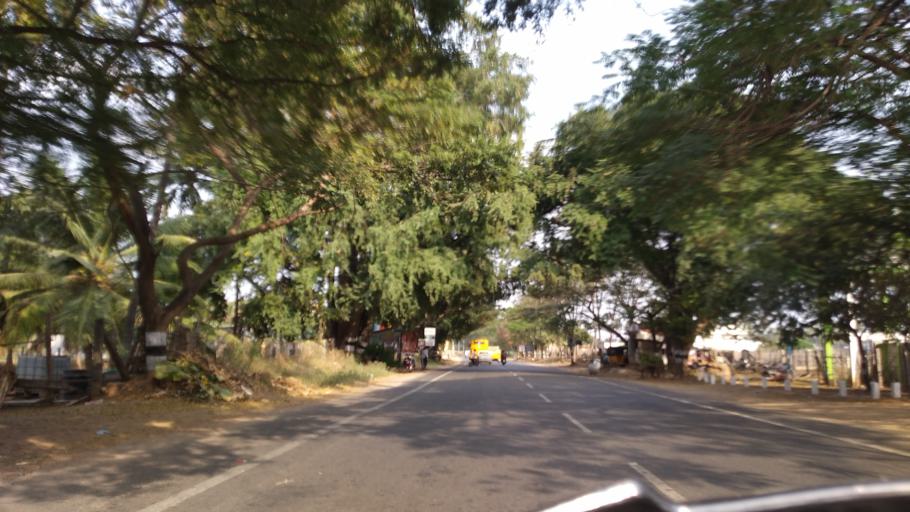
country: IN
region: Tamil Nadu
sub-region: Coimbatore
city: Perur
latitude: 10.9731
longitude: 76.8733
